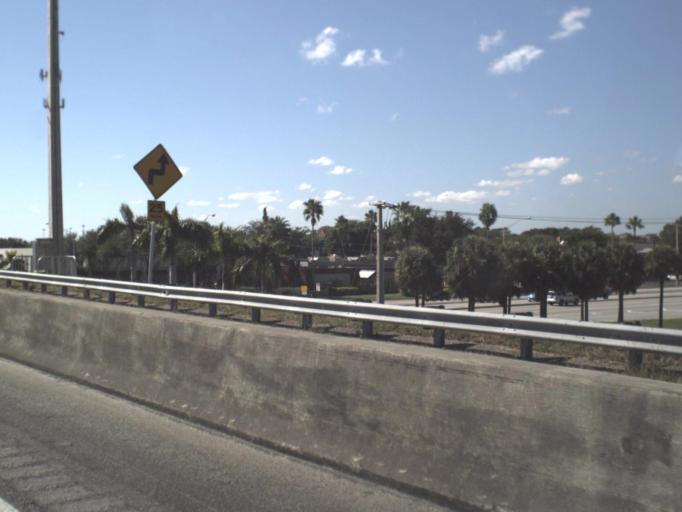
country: US
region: Florida
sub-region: Miami-Dade County
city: The Crossings
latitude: 25.6870
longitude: -80.3893
